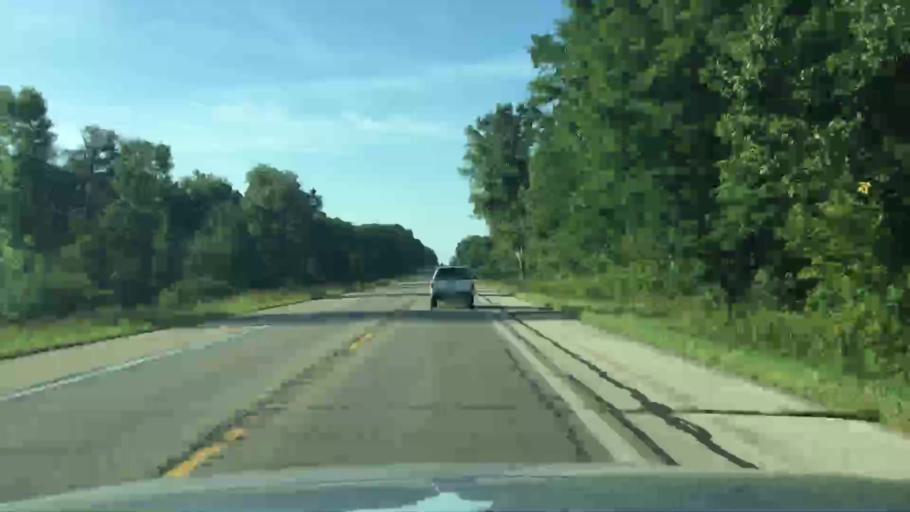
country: US
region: Michigan
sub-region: Jackson County
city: Vandercook Lake
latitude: 42.0949
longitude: -84.3639
